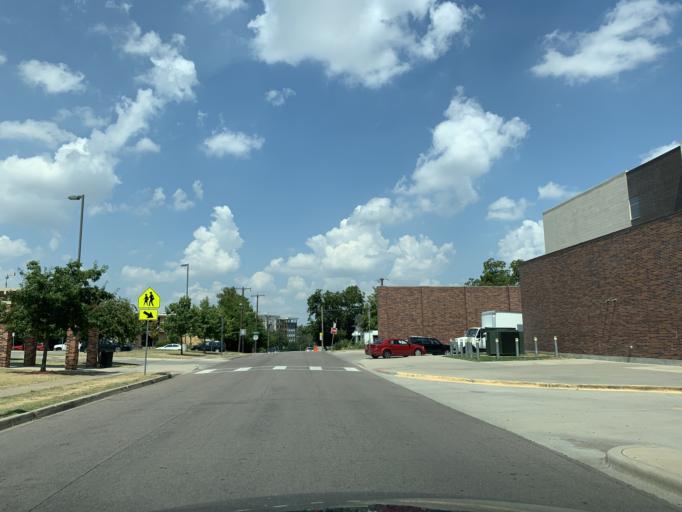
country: US
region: Texas
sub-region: Dallas County
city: Dallas
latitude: 32.7481
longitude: -96.8212
